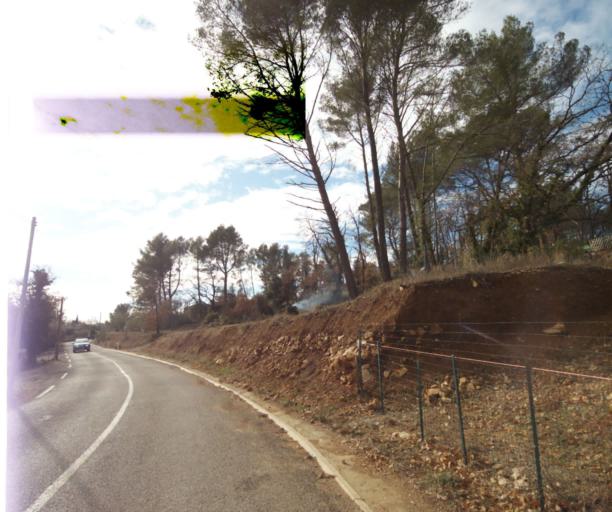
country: FR
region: Provence-Alpes-Cote d'Azur
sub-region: Departement du Var
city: Trans-en-Provence
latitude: 43.5105
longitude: 6.4935
